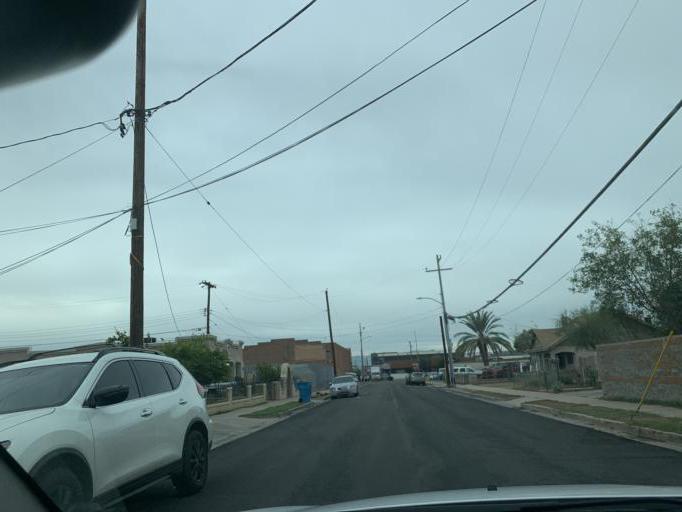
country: US
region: Arizona
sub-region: Maricopa County
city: Phoenix
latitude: 33.4525
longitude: -112.0523
